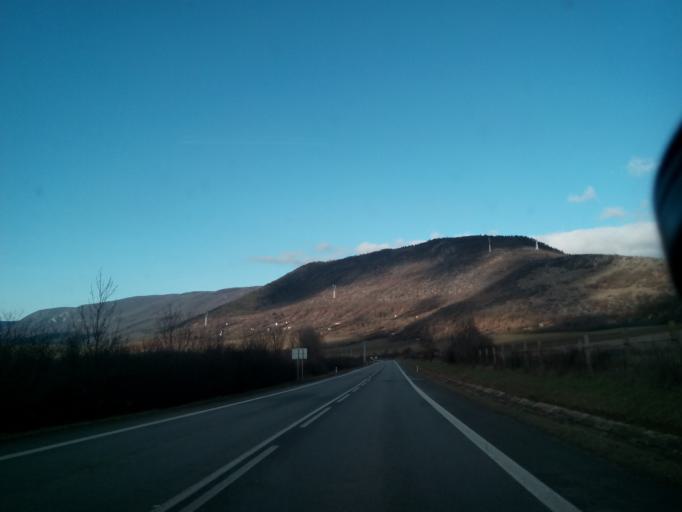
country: SK
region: Kosicky
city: Medzev
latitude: 48.6062
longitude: 20.8707
